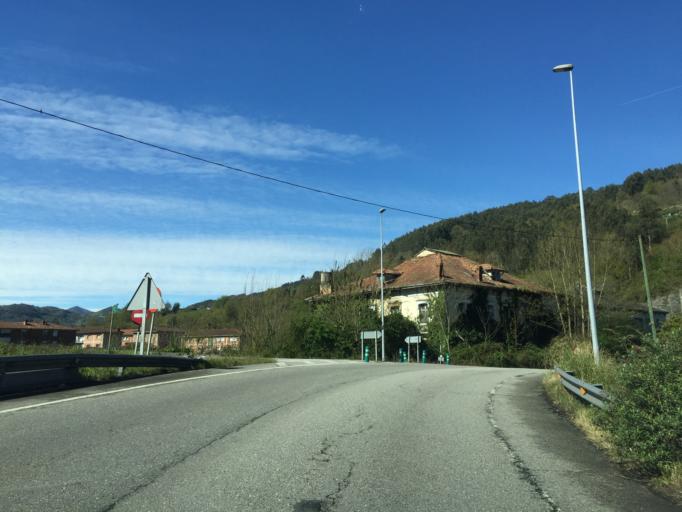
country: ES
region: Asturias
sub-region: Province of Asturias
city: Castandiello
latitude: 43.3531
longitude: -5.9636
